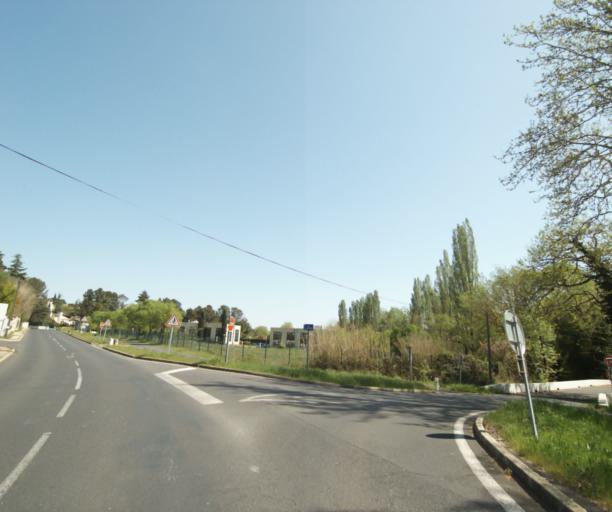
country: FR
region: Languedoc-Roussillon
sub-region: Departement de l'Herault
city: Montferrier-sur-Lez
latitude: 43.6530
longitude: 3.8587
